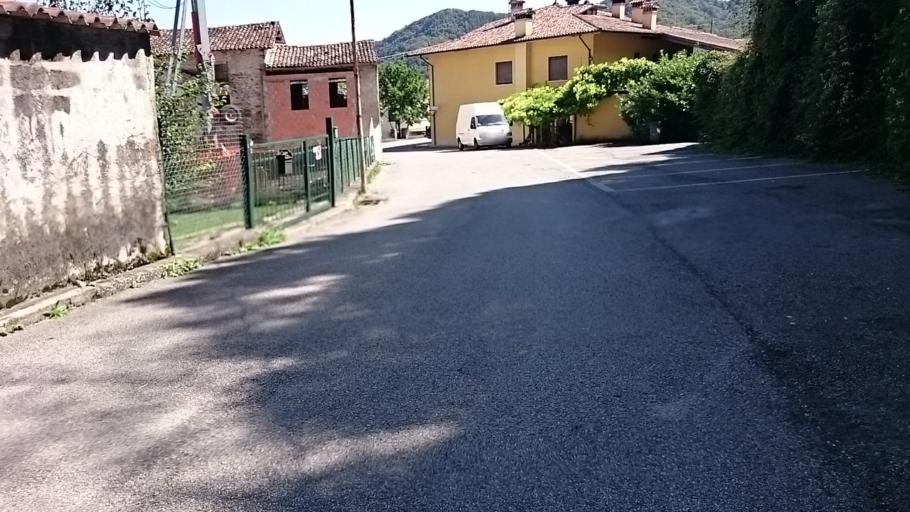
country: IT
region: Veneto
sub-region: Provincia di Treviso
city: Follina
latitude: 45.9377
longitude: 12.1254
